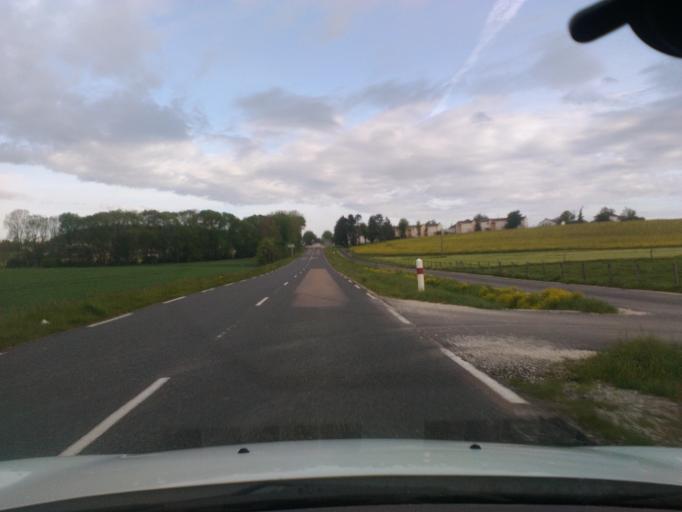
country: FR
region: Champagne-Ardenne
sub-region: Departement de la Haute-Marne
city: Lavilleneuve-au-Roi
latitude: 48.2208
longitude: 4.8980
